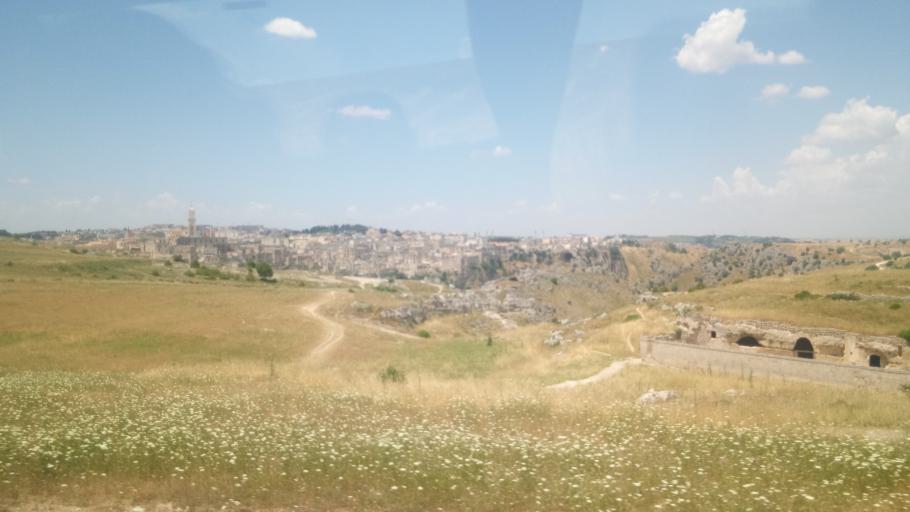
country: IT
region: Basilicate
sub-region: Provincia di Matera
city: Matera
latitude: 40.6664
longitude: 16.6216
